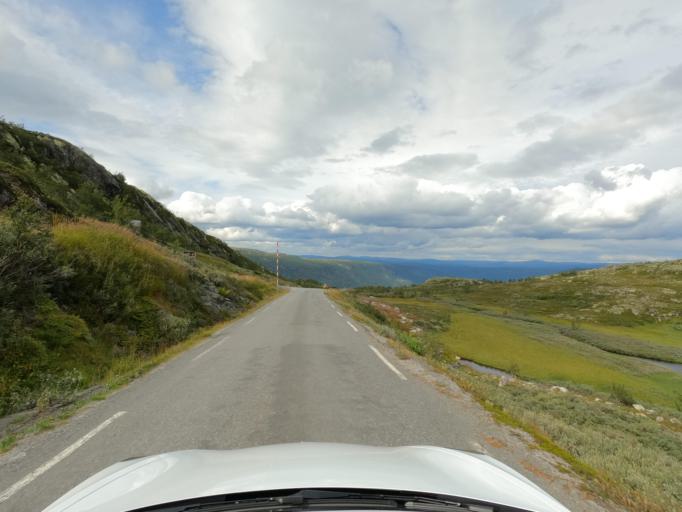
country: NO
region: Telemark
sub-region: Tinn
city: Rjukan
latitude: 59.8572
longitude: 8.6869
